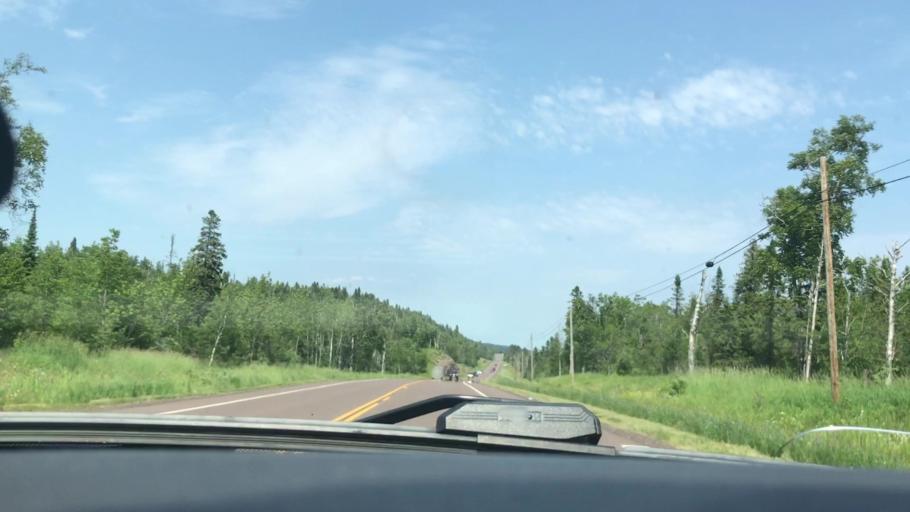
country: US
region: Minnesota
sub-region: Lake County
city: Silver Bay
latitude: 47.4324
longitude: -91.0845
